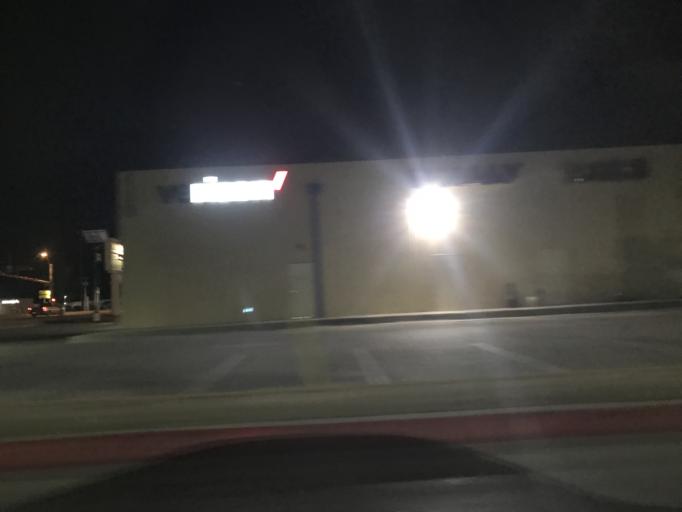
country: US
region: Texas
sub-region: Taylor County
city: Abilene
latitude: 32.4793
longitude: -99.6975
